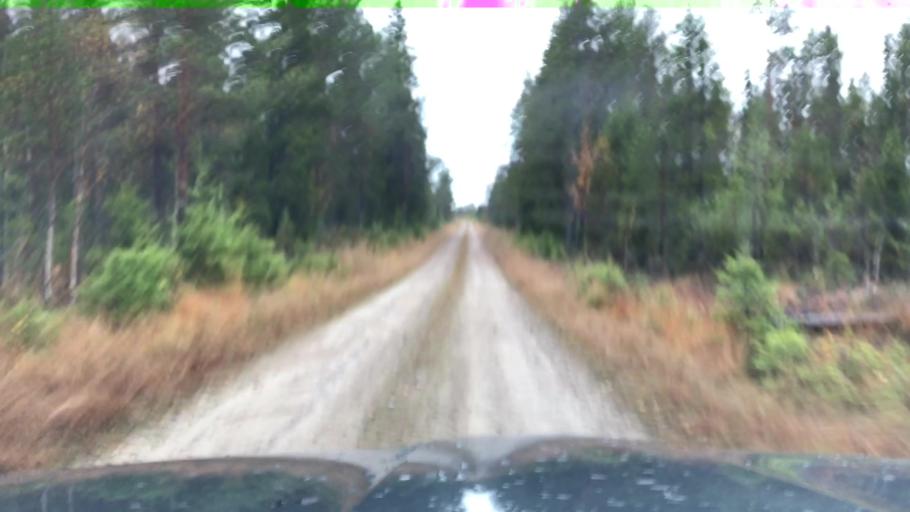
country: NO
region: Hedmark
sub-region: Trysil
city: Innbygda
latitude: 60.9273
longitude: 12.6434
